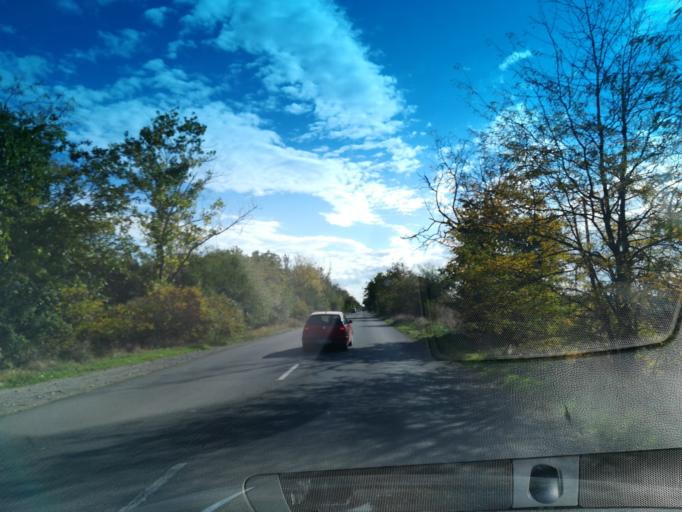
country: BG
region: Stara Zagora
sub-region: Obshtina Stara Zagora
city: Stara Zagora
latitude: 42.3722
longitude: 25.6526
